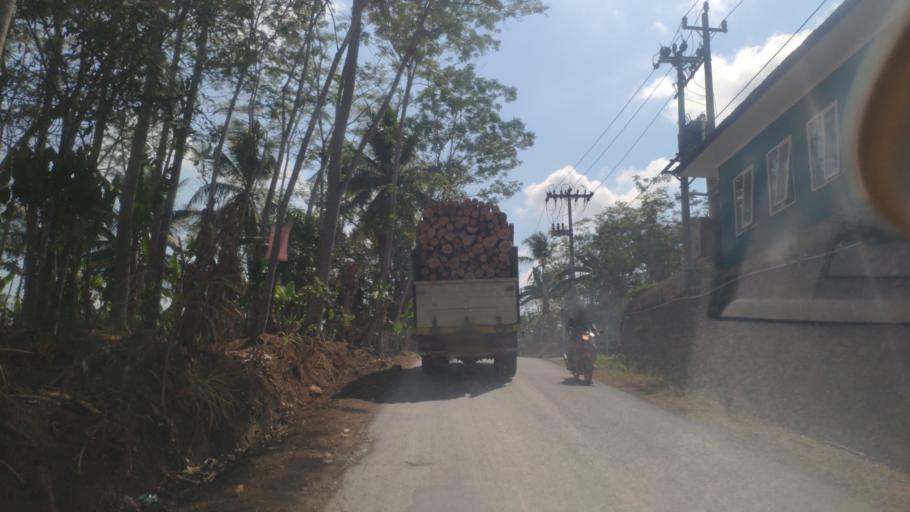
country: ID
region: Central Java
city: Gombong
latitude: -7.4223
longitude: 109.6455
